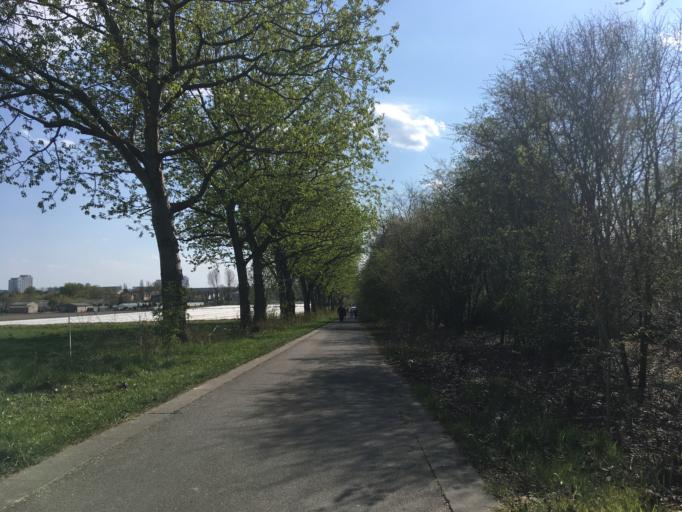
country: DE
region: Berlin
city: Wartenberg
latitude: 52.5837
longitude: 13.5152
